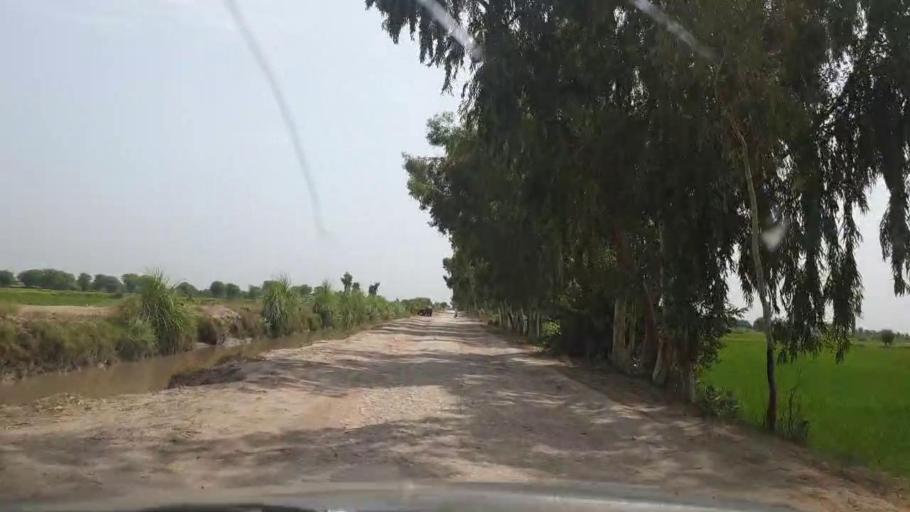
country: PK
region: Sindh
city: Ratodero
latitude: 27.8802
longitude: 68.3419
